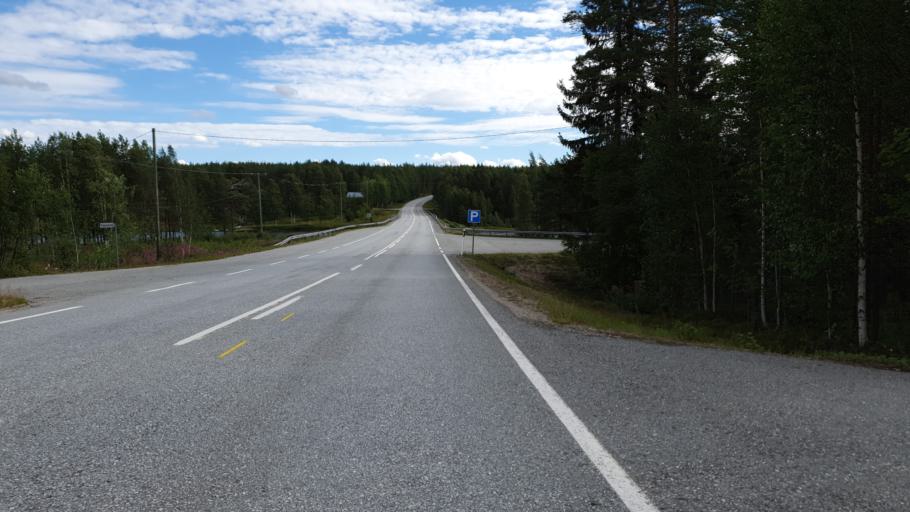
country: FI
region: Kainuu
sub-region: Kehys-Kainuu
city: Kuhmo
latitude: 64.4875
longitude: 29.8084
